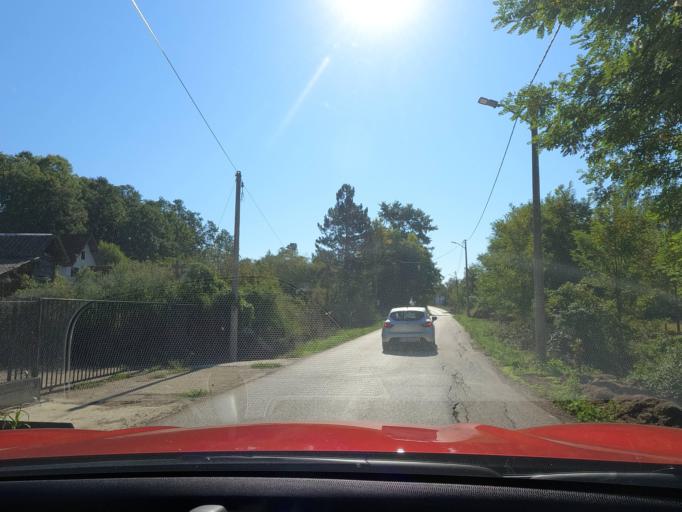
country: RS
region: Central Serbia
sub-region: Raski Okrug
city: Kraljevo
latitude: 43.7691
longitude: 20.6640
